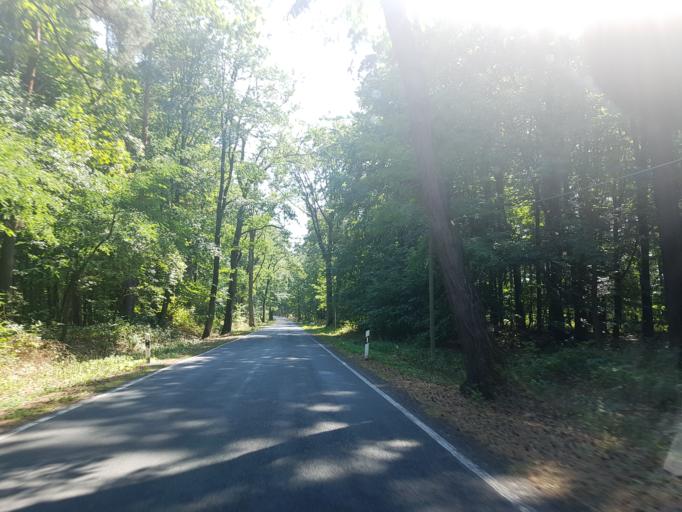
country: DE
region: Brandenburg
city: Wiesenburg
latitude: 52.0181
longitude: 12.3779
